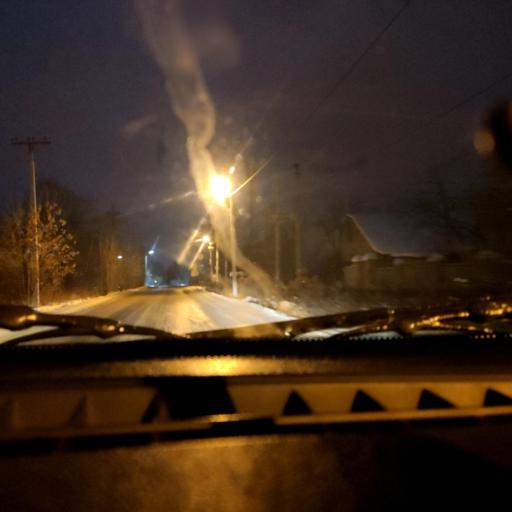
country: RU
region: Bashkortostan
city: Ufa
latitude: 54.6566
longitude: 56.0585
